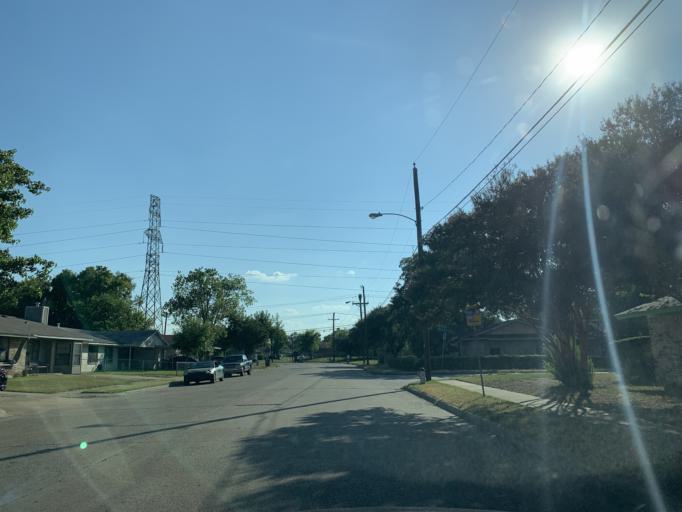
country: US
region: Texas
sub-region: Dallas County
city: Hutchins
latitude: 32.6593
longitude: -96.7660
